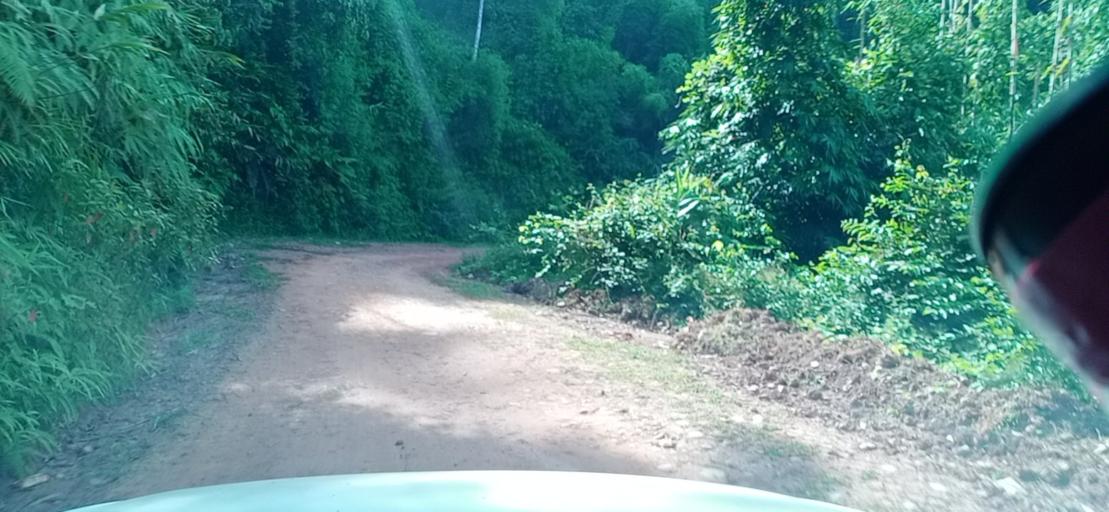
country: TH
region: Changwat Bueng Kan
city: Pak Khat
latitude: 18.6623
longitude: 103.1963
